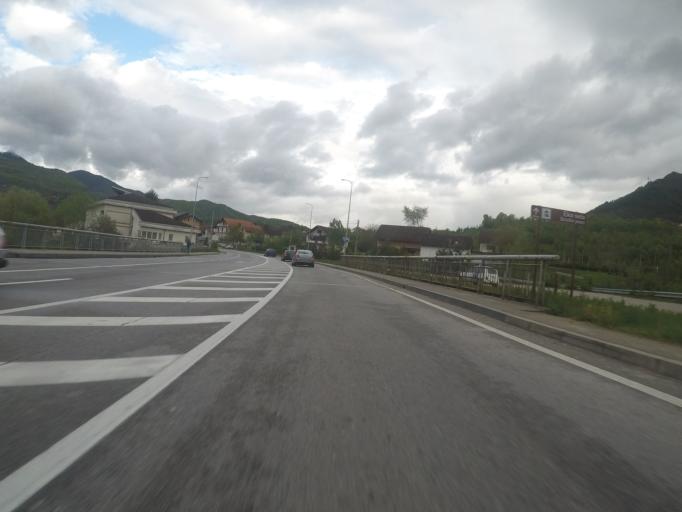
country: BA
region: Federation of Bosnia and Herzegovina
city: Konjic
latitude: 43.6837
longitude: 17.8934
